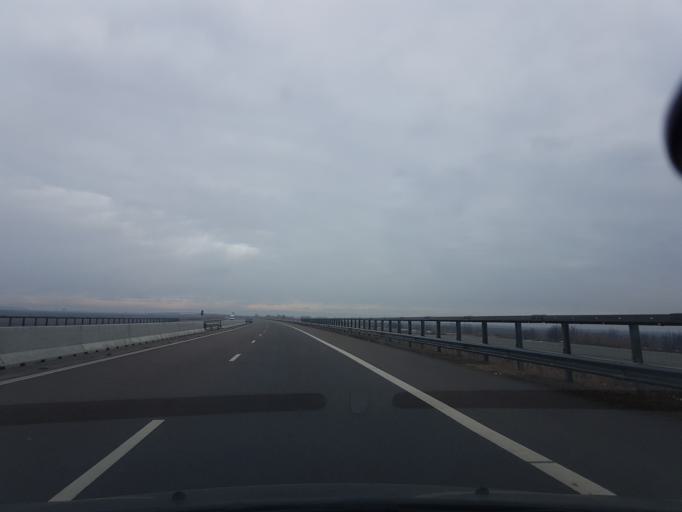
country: RO
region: Ilfov
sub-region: Comuna Gruiu
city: Gruiu
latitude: 44.7336
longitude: 26.2554
